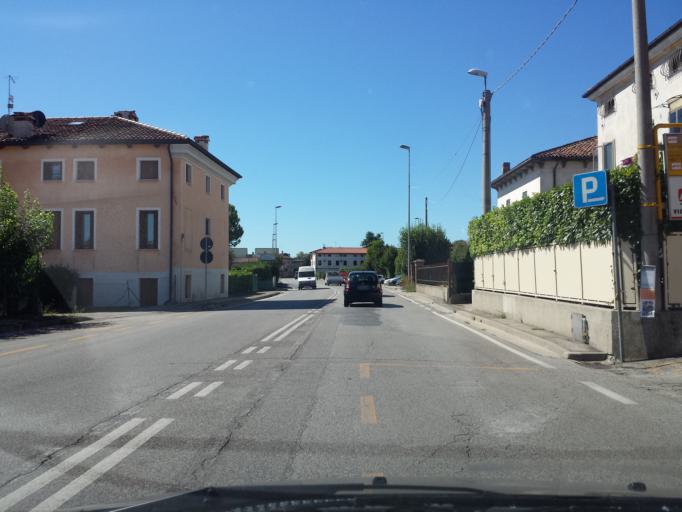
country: IT
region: Veneto
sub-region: Provincia di Vicenza
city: Vicenza
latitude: 45.5756
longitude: 11.5509
